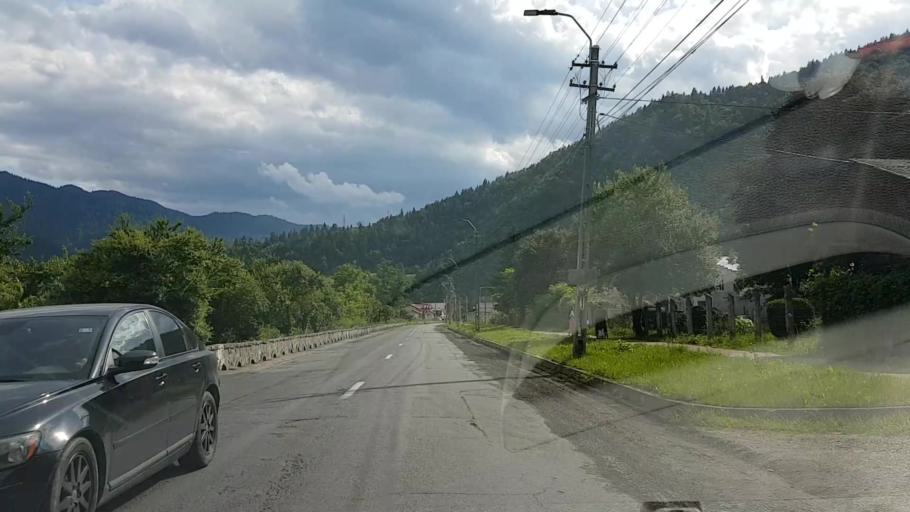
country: RO
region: Neamt
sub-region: Comuna Bicaz
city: Dodeni
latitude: 46.9230
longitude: 26.0910
